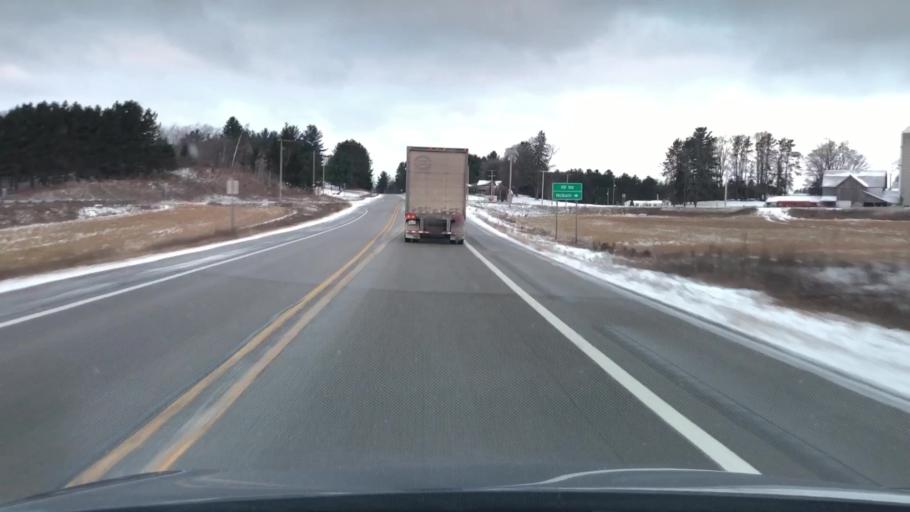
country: US
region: Michigan
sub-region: Wexford County
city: Cadillac
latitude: 44.1924
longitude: -85.3941
